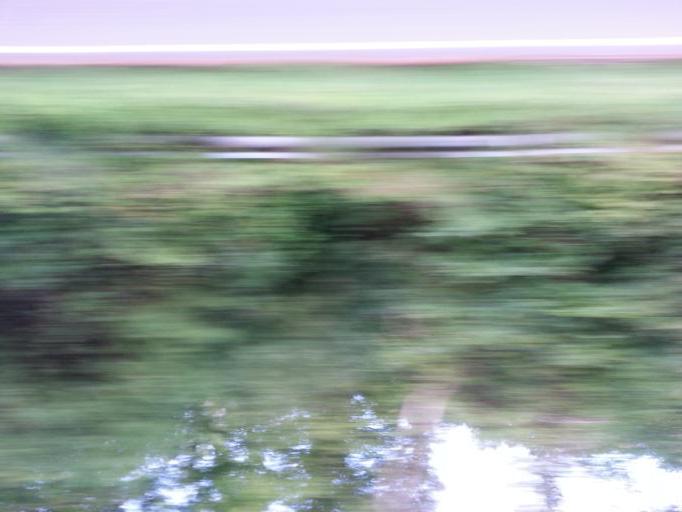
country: US
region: Tennessee
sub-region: Johnson County
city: Mountain City
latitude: 36.6202
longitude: -81.7931
